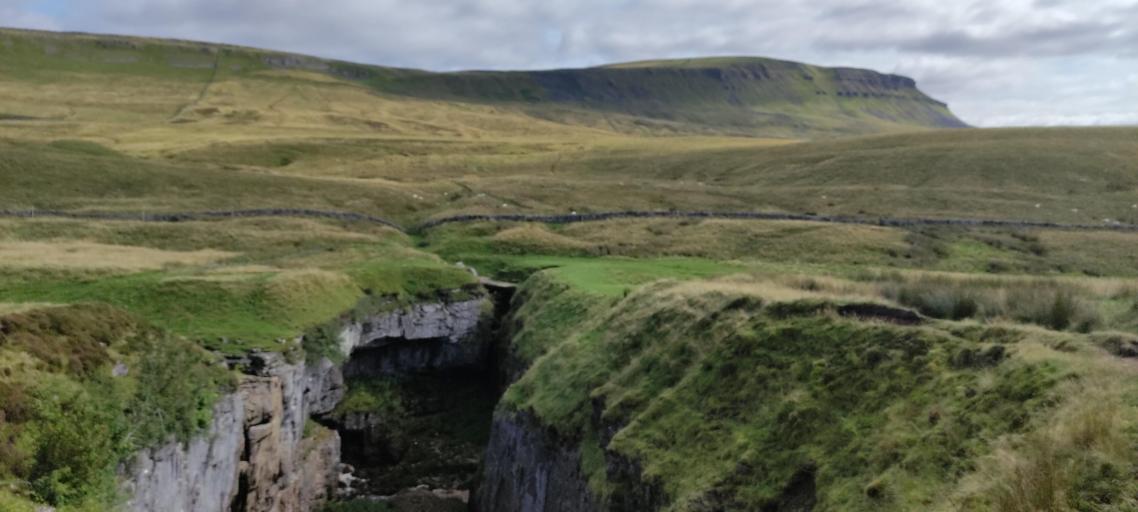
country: GB
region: England
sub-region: North Yorkshire
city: Settle
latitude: 54.1668
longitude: -2.2717
